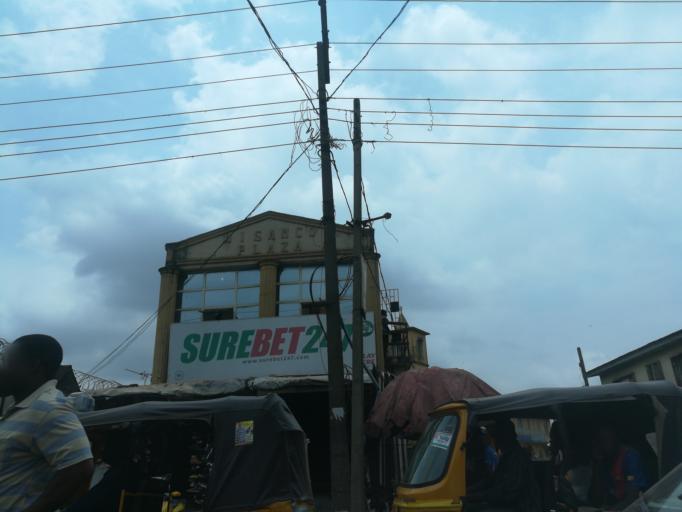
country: NG
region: Lagos
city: Agege
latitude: 6.6238
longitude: 3.3238
